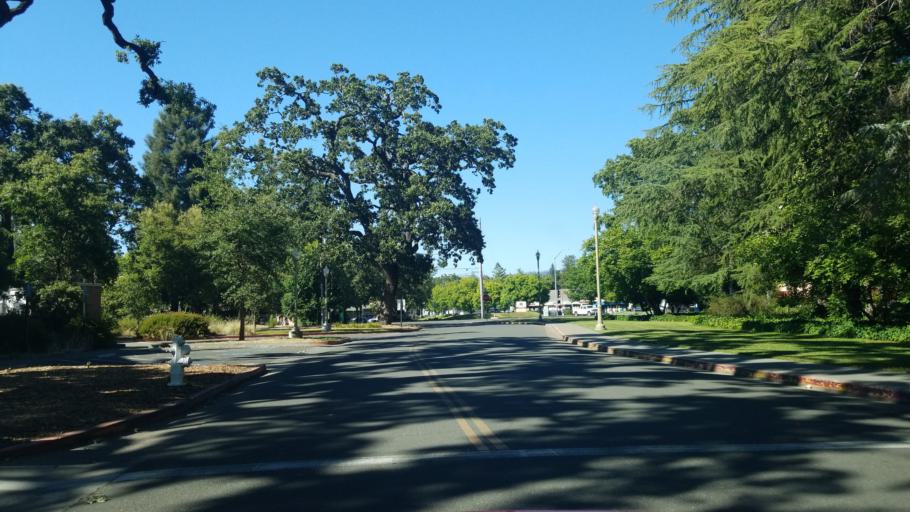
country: US
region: California
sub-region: Sonoma County
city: Santa Rosa
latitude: 38.4569
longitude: -122.7183
